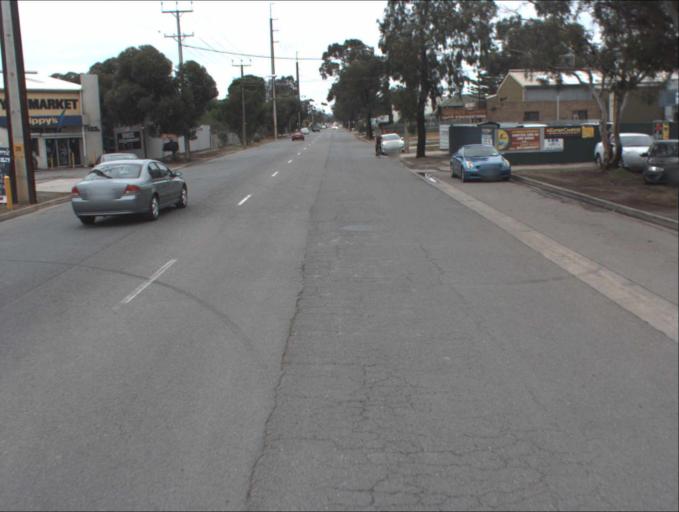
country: AU
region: South Australia
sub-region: Port Adelaide Enfield
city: Enfield
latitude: -34.8367
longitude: 138.5880
